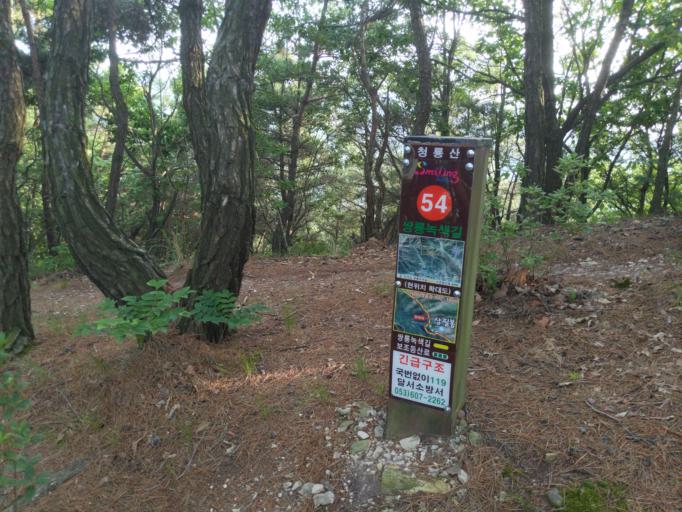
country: KR
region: Daegu
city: Hwawon
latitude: 35.7832
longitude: 128.5466
